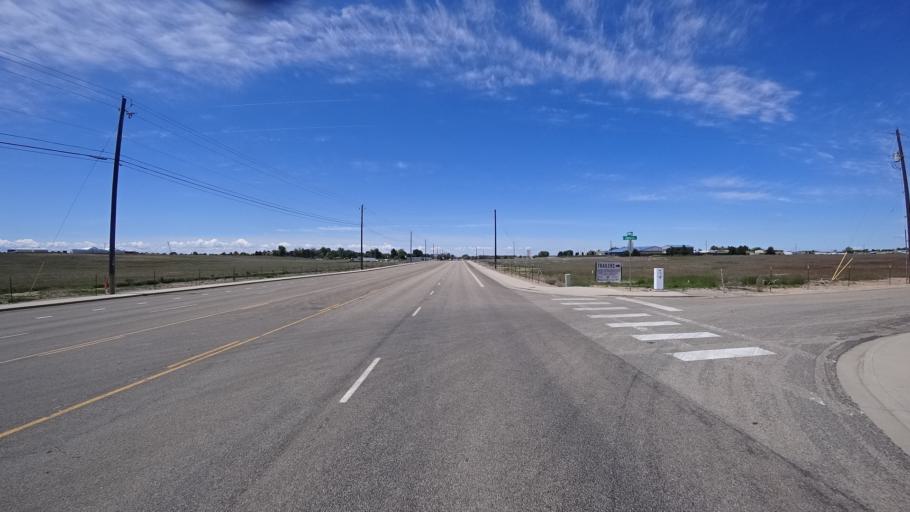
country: US
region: Idaho
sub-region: Ada County
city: Garden City
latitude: 43.5753
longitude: -116.2558
